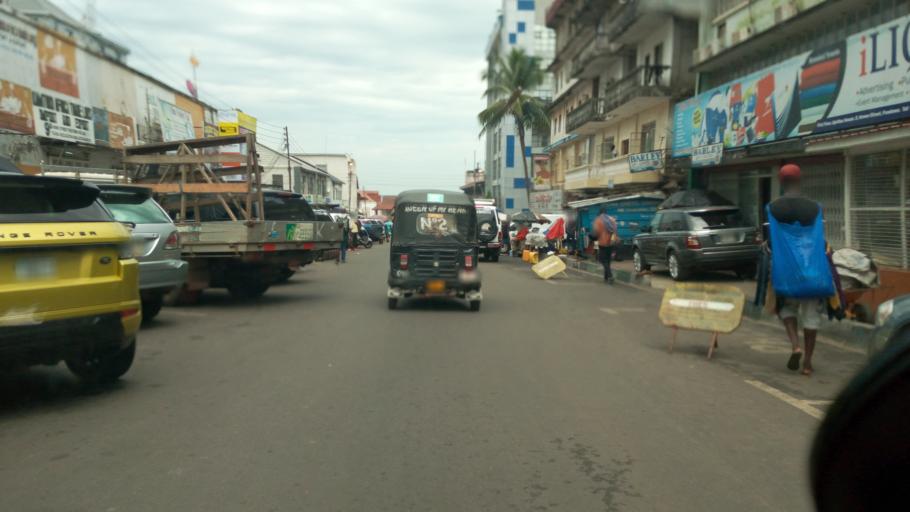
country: SL
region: Western Area
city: Freetown
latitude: 8.4898
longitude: -13.2337
